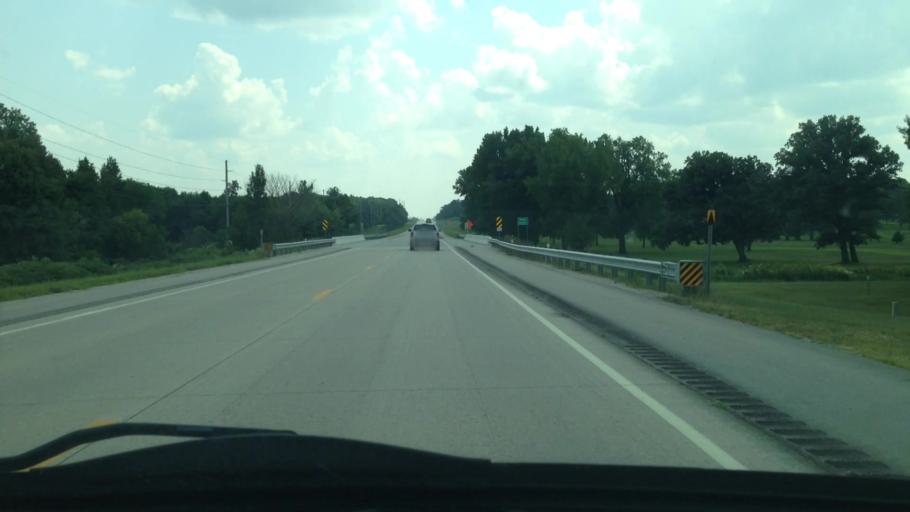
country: US
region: Minnesota
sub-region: Fillmore County
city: Spring Valley
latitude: 43.6276
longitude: -92.3895
